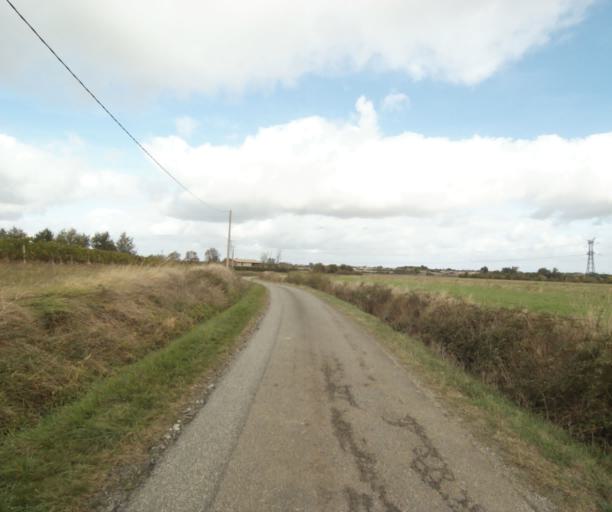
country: FR
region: Midi-Pyrenees
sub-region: Departement du Tarn-et-Garonne
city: Finhan
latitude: 43.8894
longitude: 1.1223
